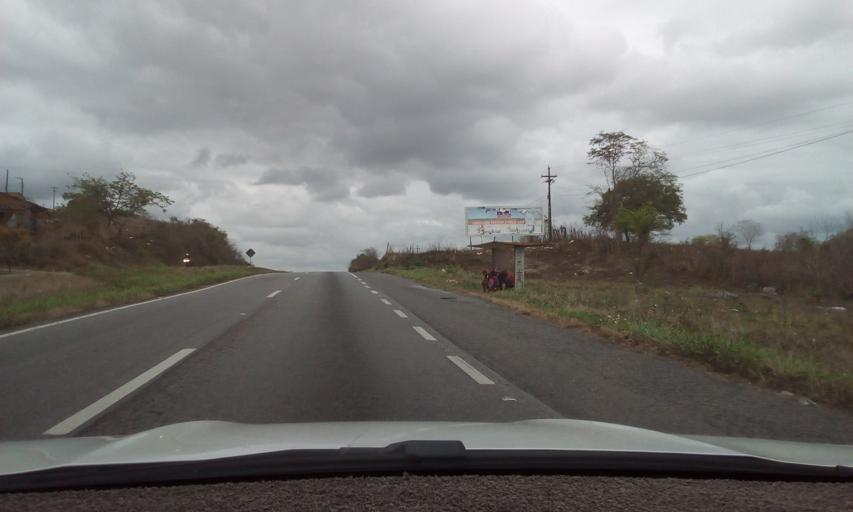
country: BR
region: Paraiba
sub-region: Massaranduba
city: Massaranduba
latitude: -7.2692
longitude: -35.7911
